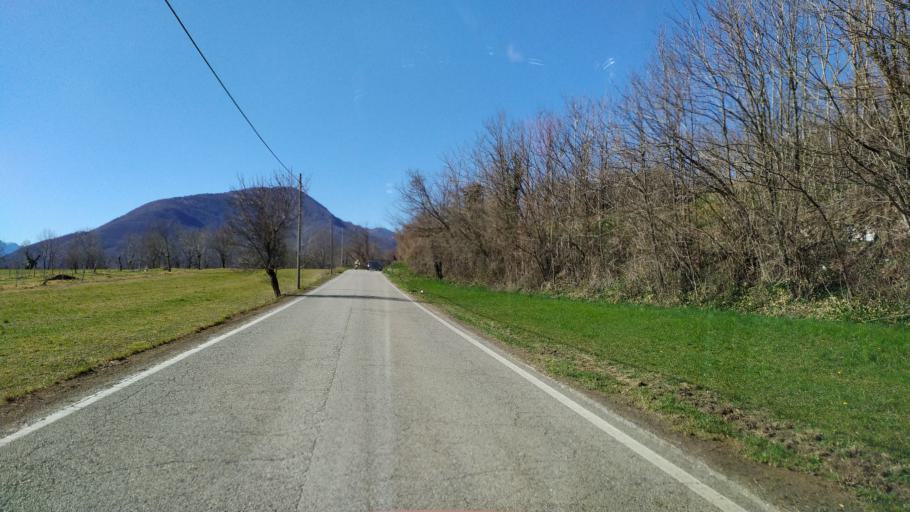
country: IT
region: Veneto
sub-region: Provincia di Vicenza
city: Chiuppano
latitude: 45.7659
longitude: 11.4767
